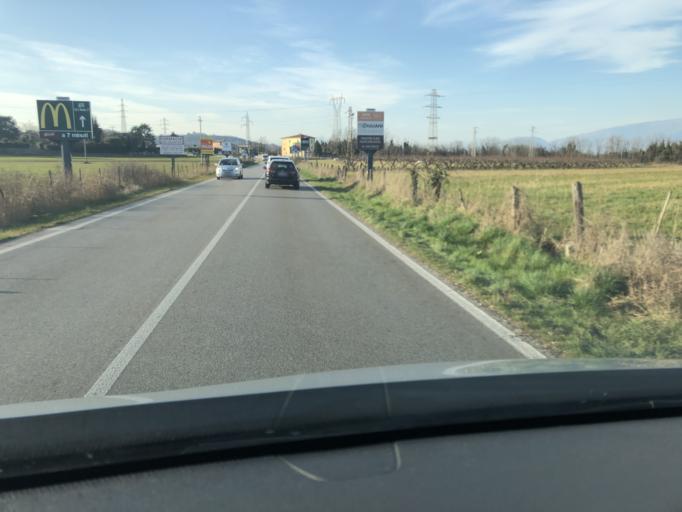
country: IT
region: Veneto
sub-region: Provincia di Verona
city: Bussolengo
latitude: 45.4744
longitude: 10.8392
